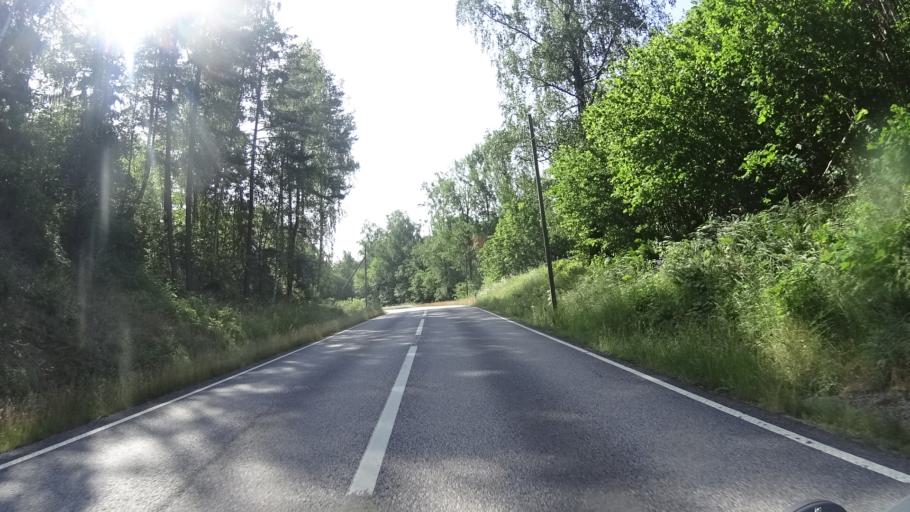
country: SE
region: Kalmar
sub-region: Vasterviks Kommun
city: Overum
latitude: 58.0211
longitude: 16.2432
